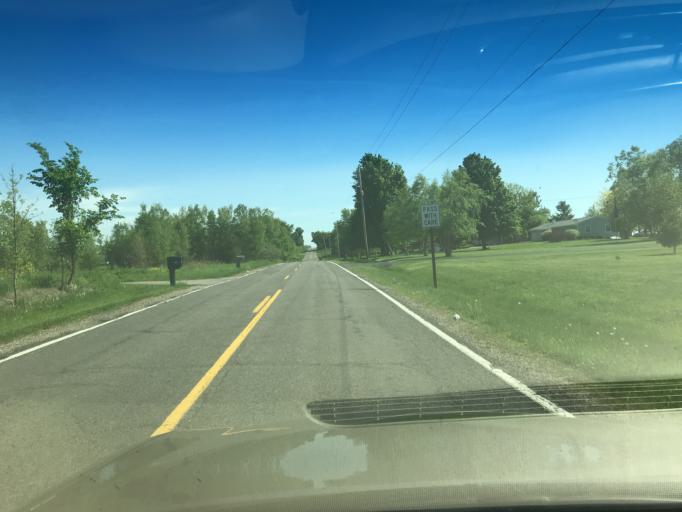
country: US
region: Michigan
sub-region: Ingham County
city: Mason
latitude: 42.5570
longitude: -84.4627
